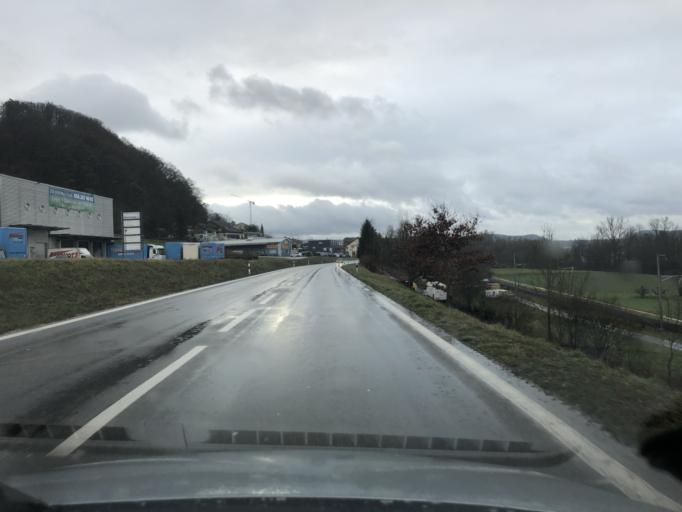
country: CH
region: Aargau
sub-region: Bezirk Zurzach
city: Klingnau
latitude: 47.5914
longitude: 8.2401
